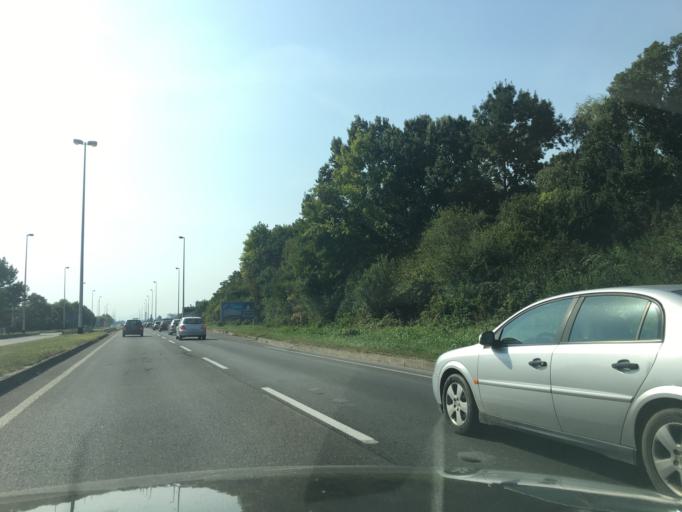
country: HR
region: Grad Zagreb
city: Dubrava
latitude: 45.8021
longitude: 16.0627
